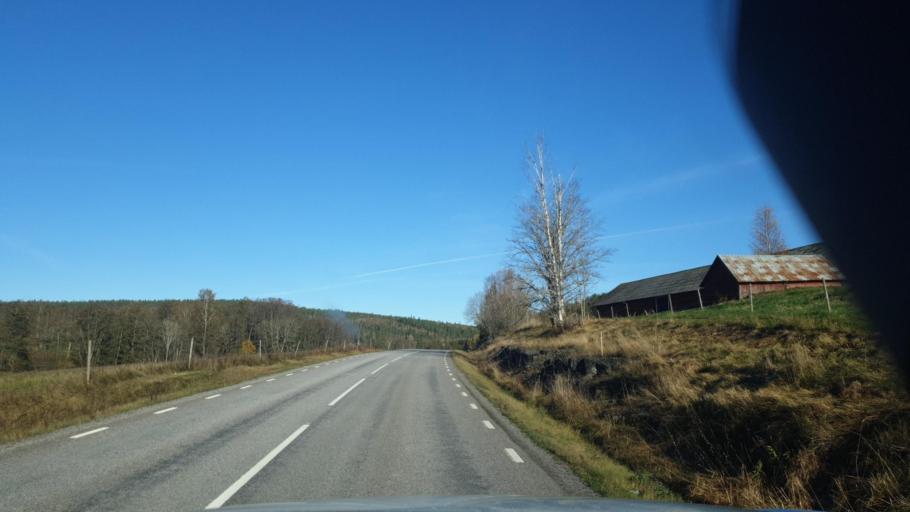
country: SE
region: Vaermland
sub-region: Grums Kommun
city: Grums
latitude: 59.3963
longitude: 13.0706
